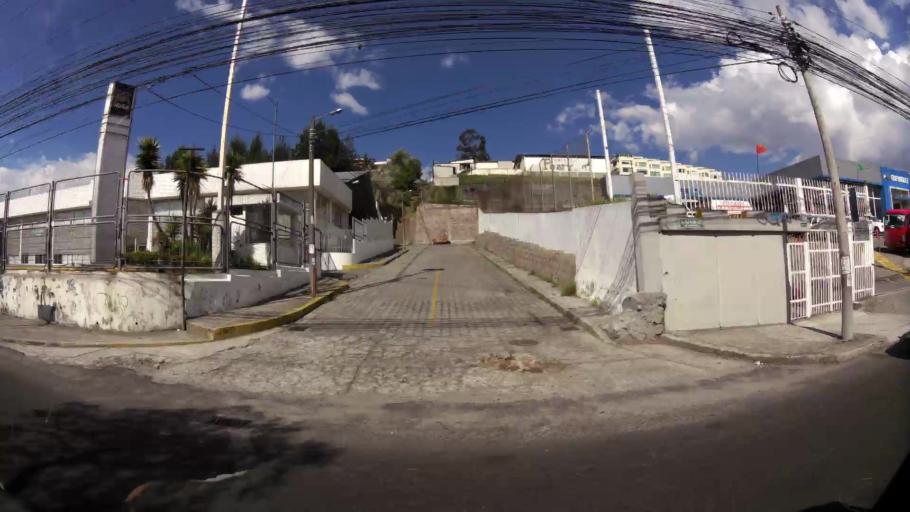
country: EC
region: Pichincha
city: Quito
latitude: -0.1182
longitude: -78.4797
